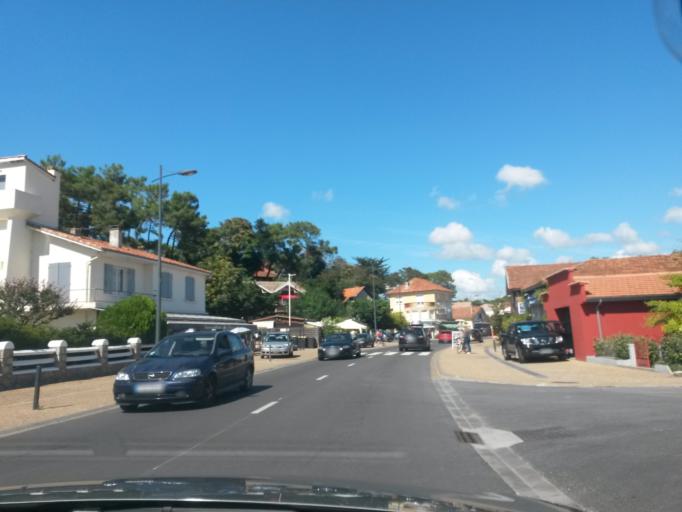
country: FR
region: Aquitaine
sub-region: Departement de la Gironde
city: Arcachon
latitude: 44.7006
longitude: -1.2299
